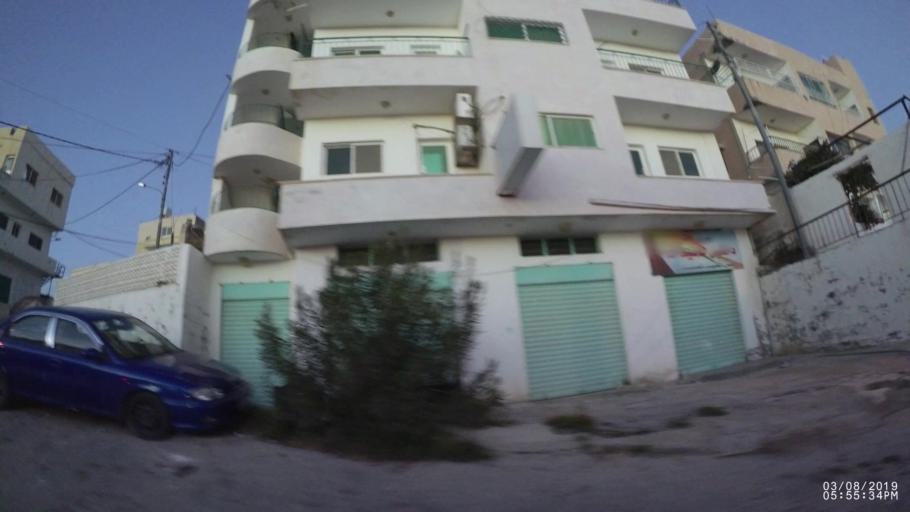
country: JO
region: Ma'an
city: Petra
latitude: 30.3235
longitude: 35.4791
